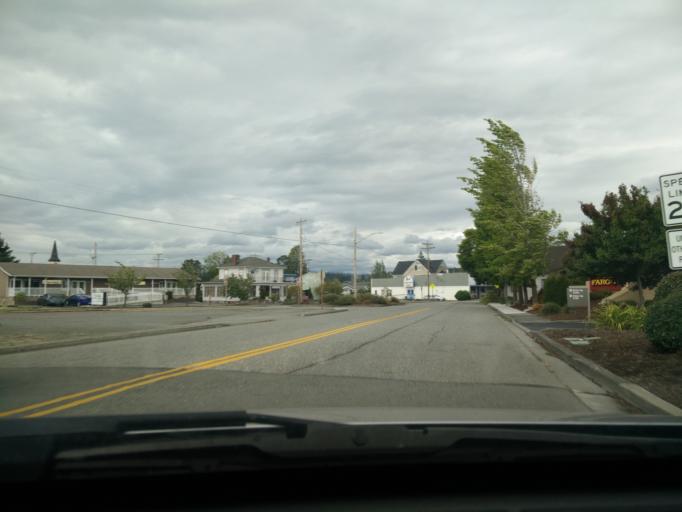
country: US
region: Washington
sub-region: Snohomish County
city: Stanwood
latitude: 48.2411
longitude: -122.3685
